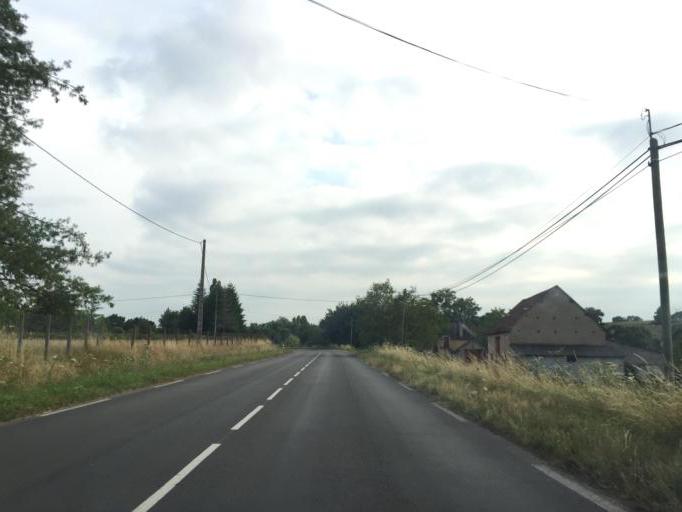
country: FR
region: Auvergne
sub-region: Departement de l'Allier
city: Molinet
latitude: 46.4613
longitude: 3.9324
